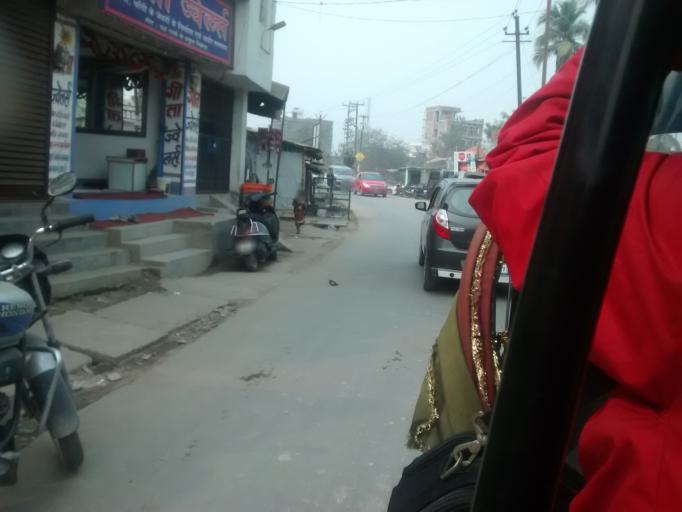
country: IN
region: Bihar
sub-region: Muzaffarpur
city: Muzaffarpur
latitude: 26.1057
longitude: 85.3938
